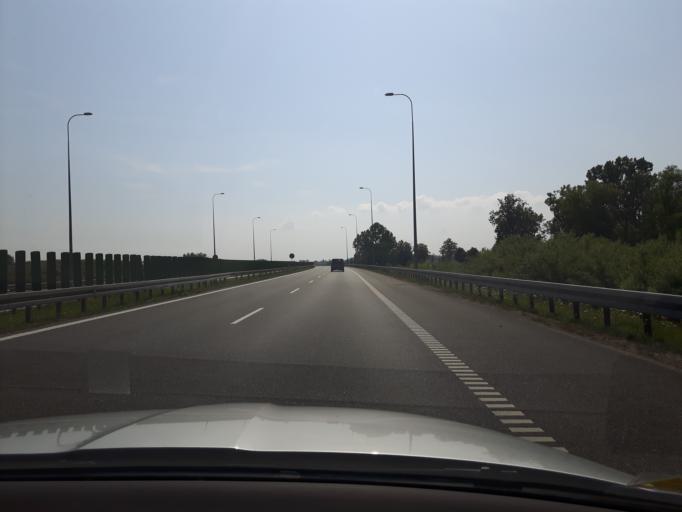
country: PL
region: Pomeranian Voivodeship
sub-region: Powiat gdanski
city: Cedry Wielkie
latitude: 54.2934
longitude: 18.8234
